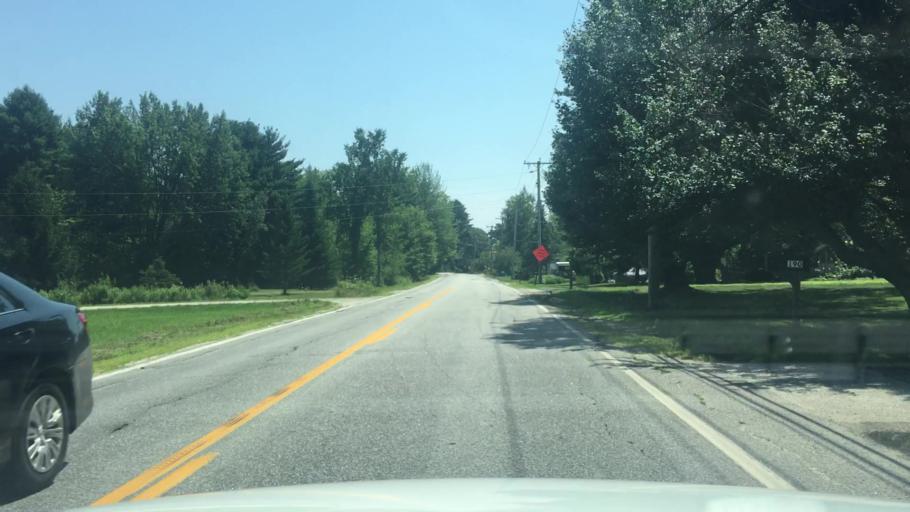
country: US
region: Maine
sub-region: Cumberland County
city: Cumberland Center
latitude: 43.7832
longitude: -70.2582
